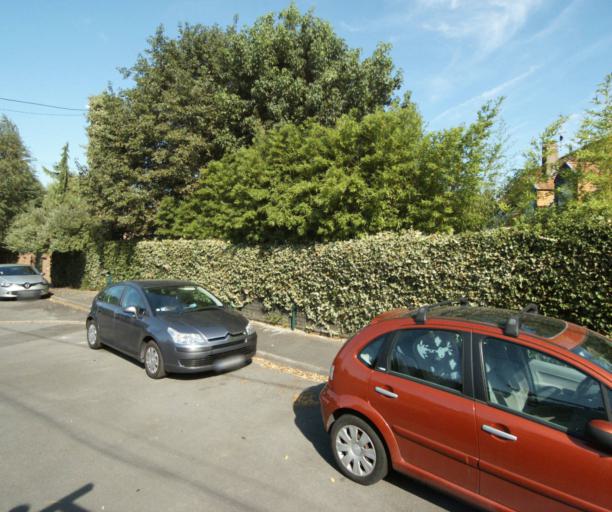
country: FR
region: Nord-Pas-de-Calais
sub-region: Departement du Nord
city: Halluin
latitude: 50.7750
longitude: 3.1322
